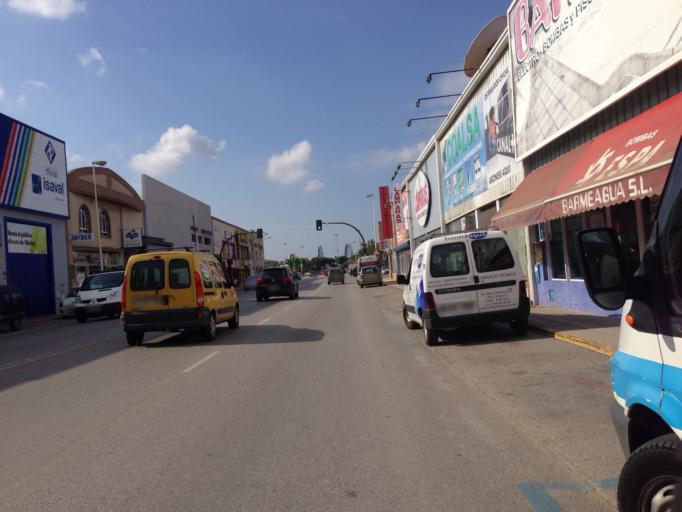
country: ES
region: Andalusia
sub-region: Provincia de Cadiz
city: Chiclana de la Frontera
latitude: 36.4271
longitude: -6.1521
